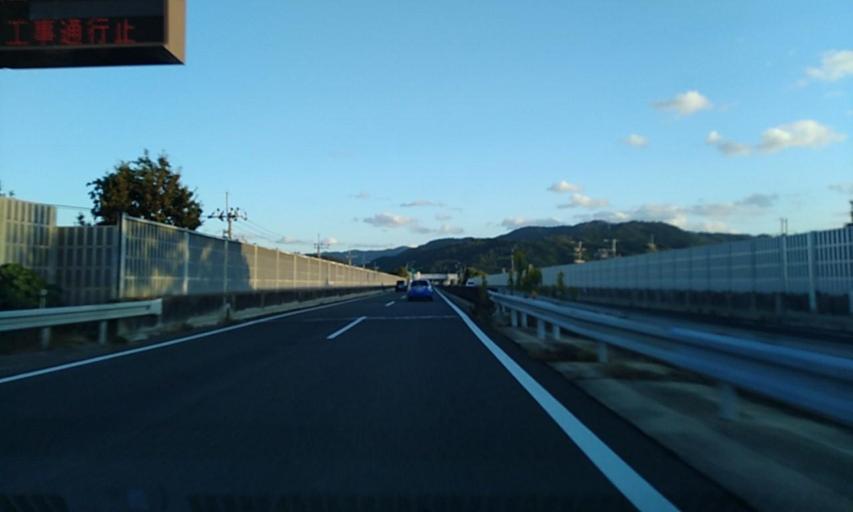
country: JP
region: Kyoto
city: Kameoka
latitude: 35.0190
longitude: 135.5537
